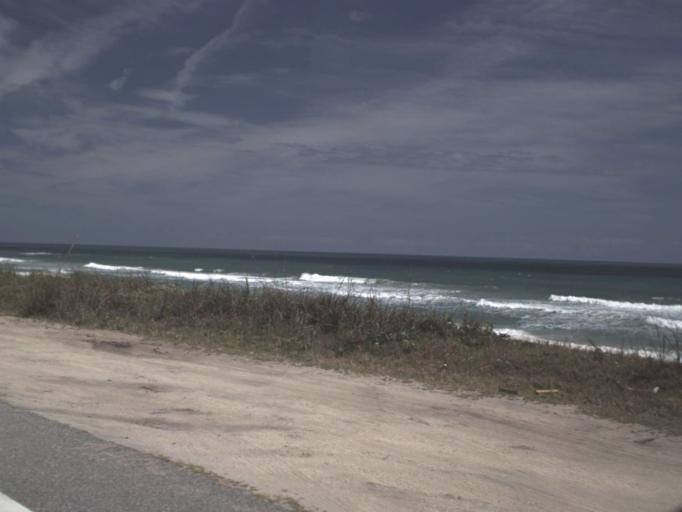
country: US
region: Florida
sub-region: Flagler County
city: Flagler Beach
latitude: 29.4435
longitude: -81.1100
